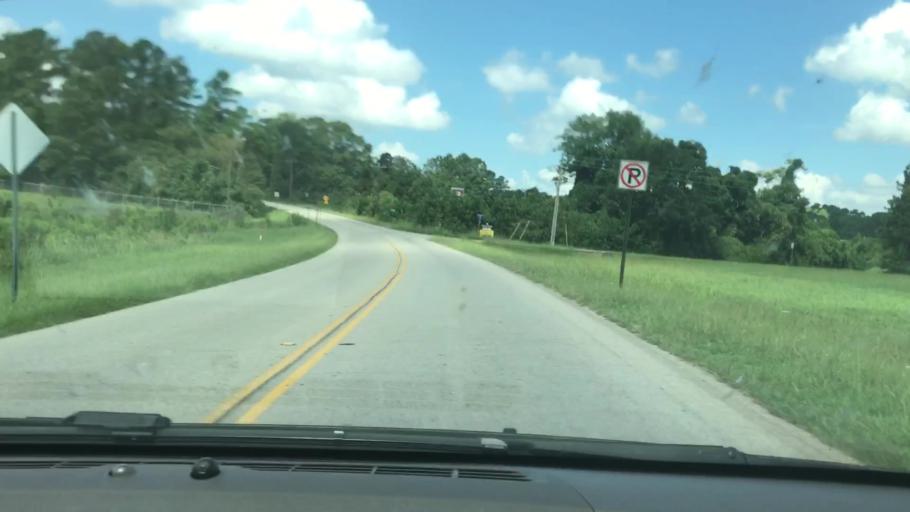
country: US
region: Georgia
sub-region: Troup County
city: La Grange
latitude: 33.0180
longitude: -85.0695
